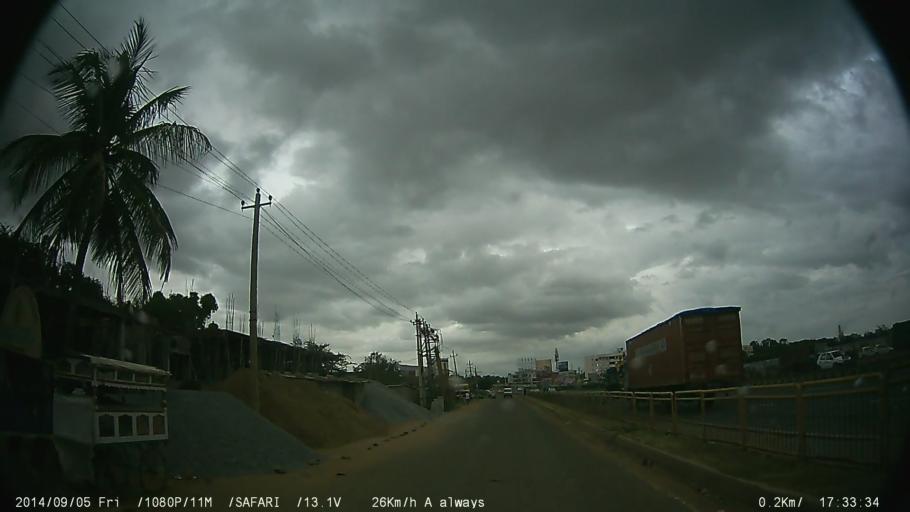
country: IN
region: Karnataka
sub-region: Bangalore Urban
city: Anekal
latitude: 12.8062
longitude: 77.6994
